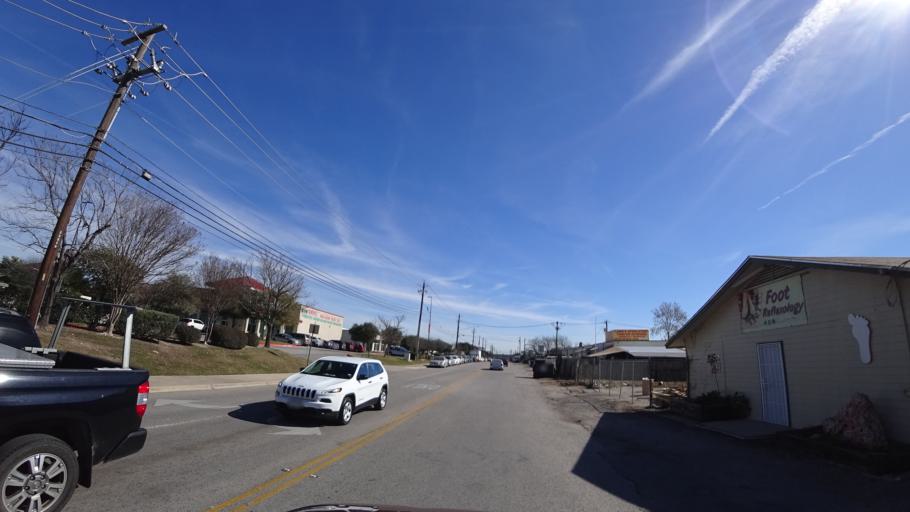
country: US
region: Texas
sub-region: Travis County
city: Wells Branch
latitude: 30.3776
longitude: -97.6886
